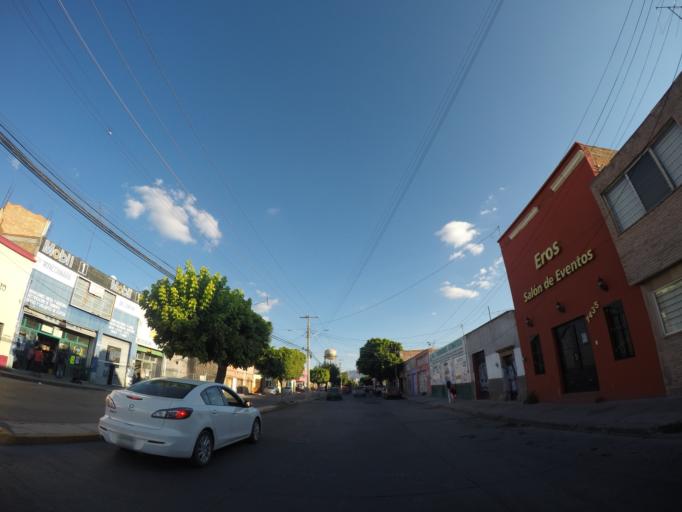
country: MX
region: San Luis Potosi
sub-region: San Luis Potosi
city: San Luis Potosi
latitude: 22.1653
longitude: -100.9805
